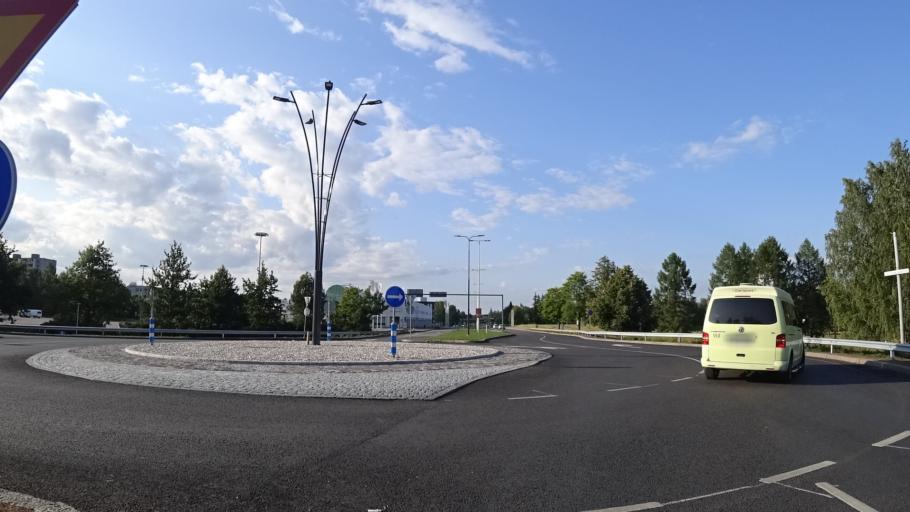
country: FI
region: South Karelia
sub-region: Imatra
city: Imatra
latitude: 61.1885
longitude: 28.7774
